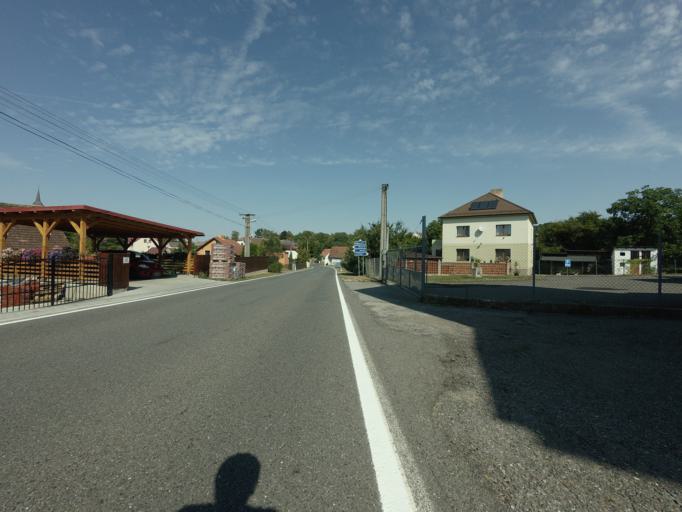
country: CZ
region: Jihocesky
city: Bernartice
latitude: 49.3872
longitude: 14.3590
